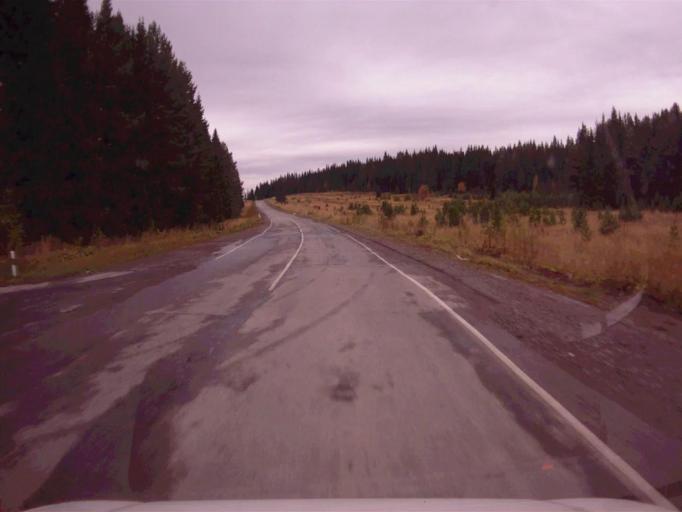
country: RU
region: Chelyabinsk
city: Nyazepetrovsk
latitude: 56.0664
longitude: 59.6453
